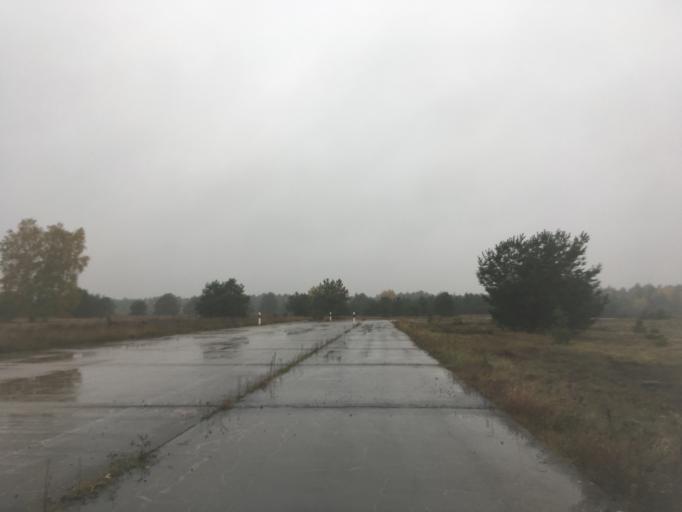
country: DE
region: Brandenburg
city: Halbe
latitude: 52.0354
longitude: 13.7297
